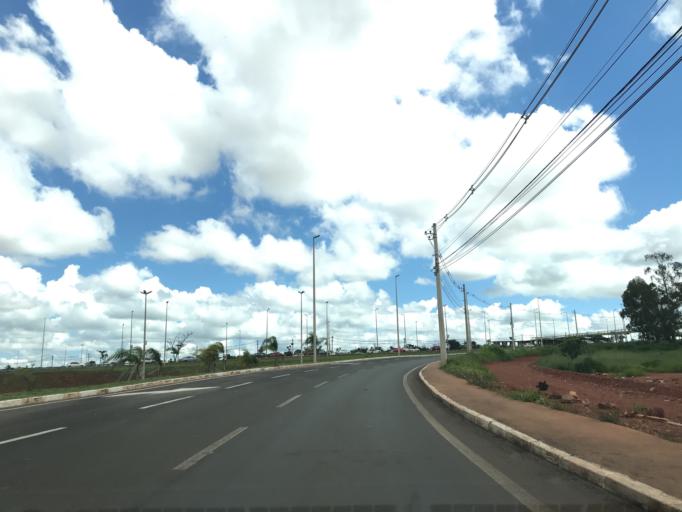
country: BR
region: Federal District
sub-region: Brasilia
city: Brasilia
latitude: -15.8142
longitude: -47.9990
